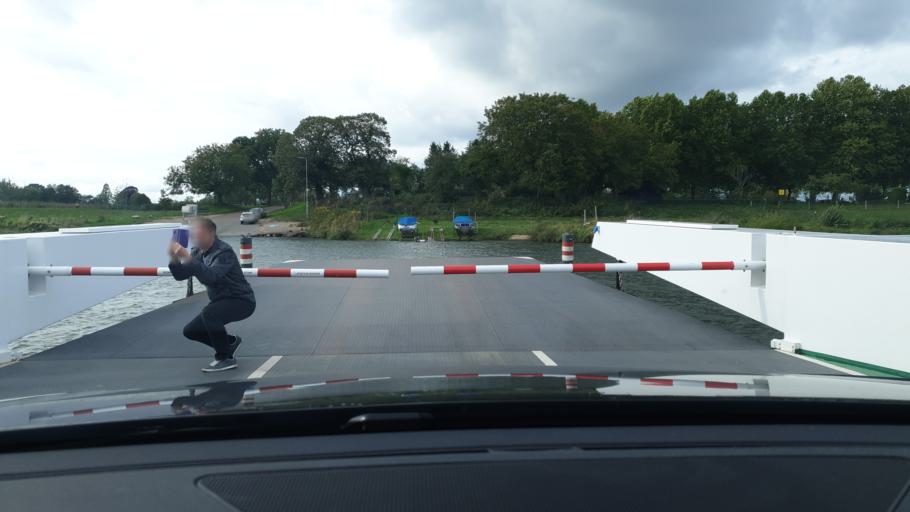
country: NL
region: Limburg
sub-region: Gemeente Venlo
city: Arcen
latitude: 51.4590
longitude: 6.1736
